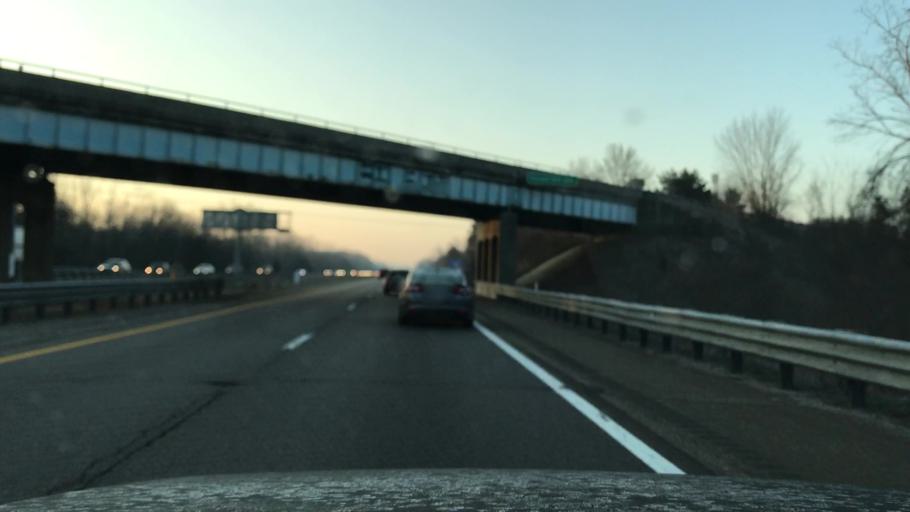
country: US
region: Michigan
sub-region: Kent County
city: East Grand Rapids
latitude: 42.9291
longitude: -85.5603
